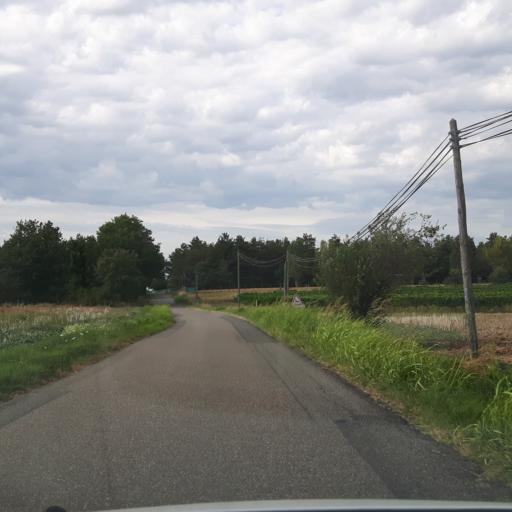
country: FR
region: Midi-Pyrenees
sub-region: Departement de la Haute-Garonne
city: Castelnau-d'Estretefonds
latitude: 43.7995
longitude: 1.3543
